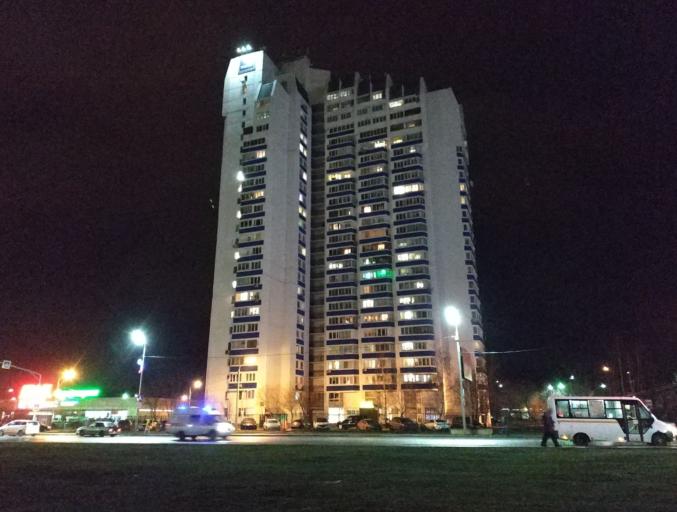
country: RU
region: Moskovskaya
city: Balashikha
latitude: 55.8261
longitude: 37.9709
